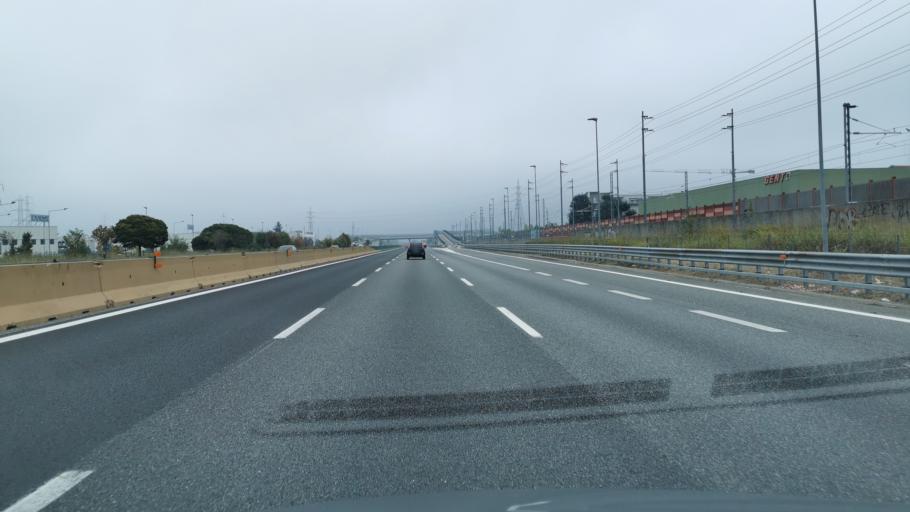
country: IT
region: Piedmont
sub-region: Provincia di Torino
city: Settimo Torinese
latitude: 45.1422
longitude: 7.7494
